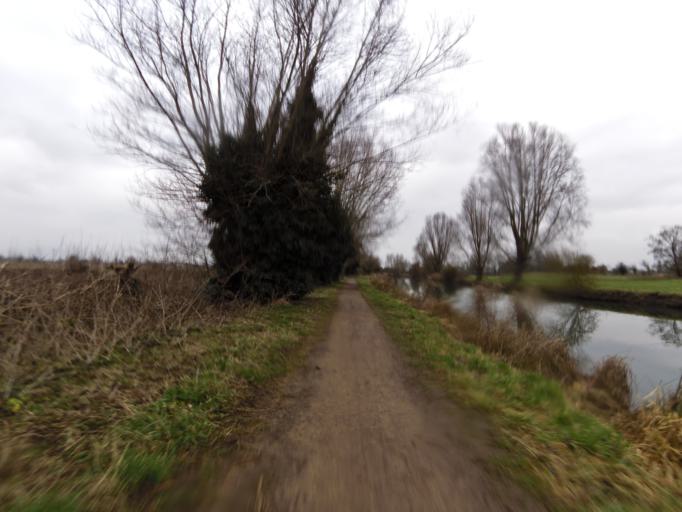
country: GB
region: England
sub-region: Cambridgeshire
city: Waterbeach
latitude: 52.2446
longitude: 0.1845
